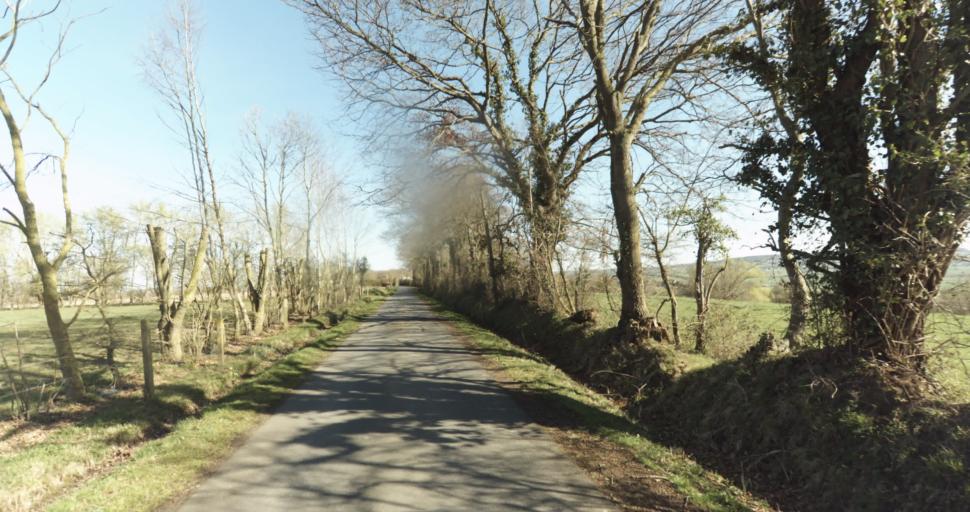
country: FR
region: Lower Normandy
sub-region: Departement du Calvados
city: Saint-Pierre-sur-Dives
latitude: 49.0459
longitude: 0.0325
